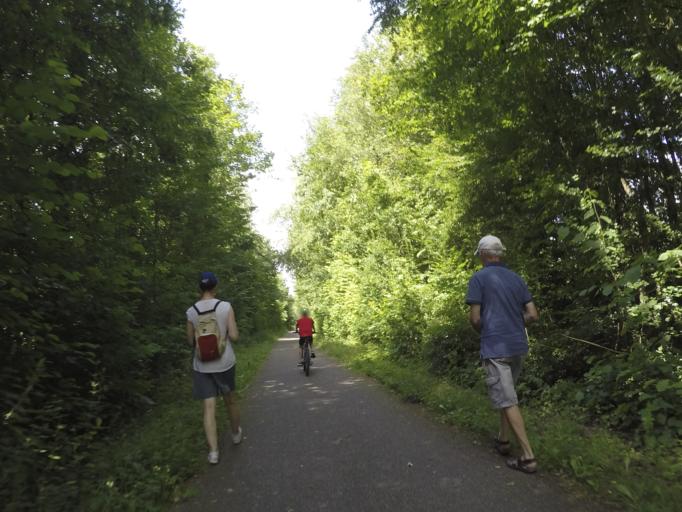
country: BE
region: Wallonia
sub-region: Province de Liege
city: Marchin
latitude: 50.4764
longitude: 5.2659
